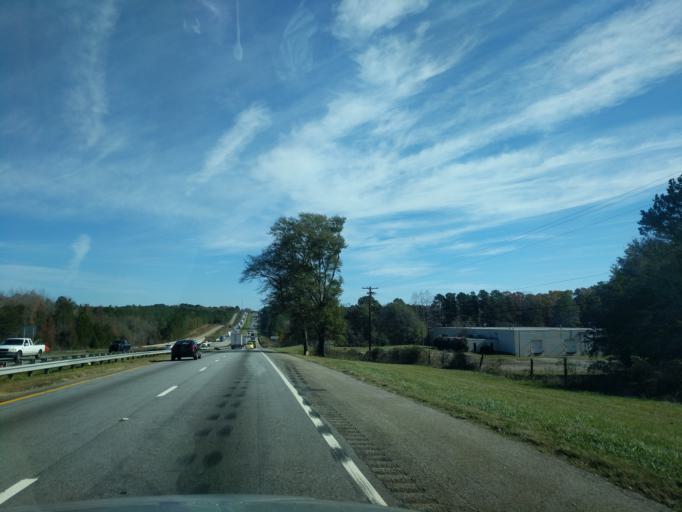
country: US
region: South Carolina
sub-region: Spartanburg County
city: Mayo
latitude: 35.0314
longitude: -81.8558
